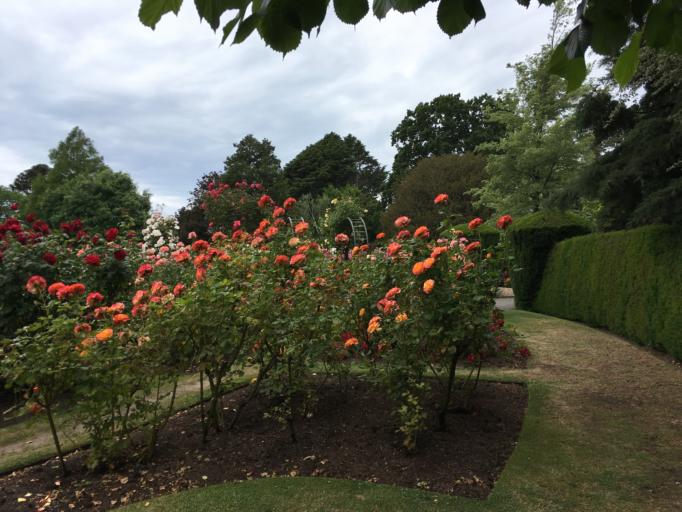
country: NZ
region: Canterbury
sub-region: Christchurch City
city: Christchurch
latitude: -43.5306
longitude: 172.6209
